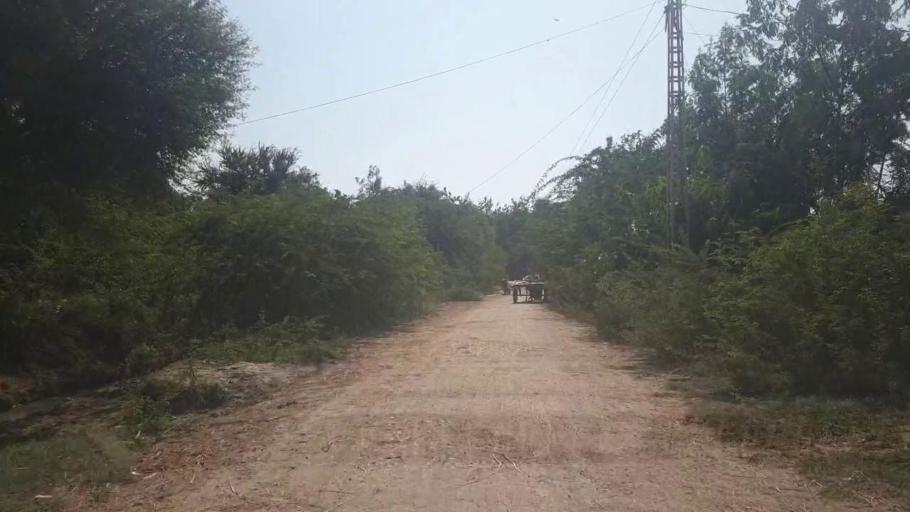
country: PK
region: Sindh
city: Badin
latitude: 24.6834
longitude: 68.8781
